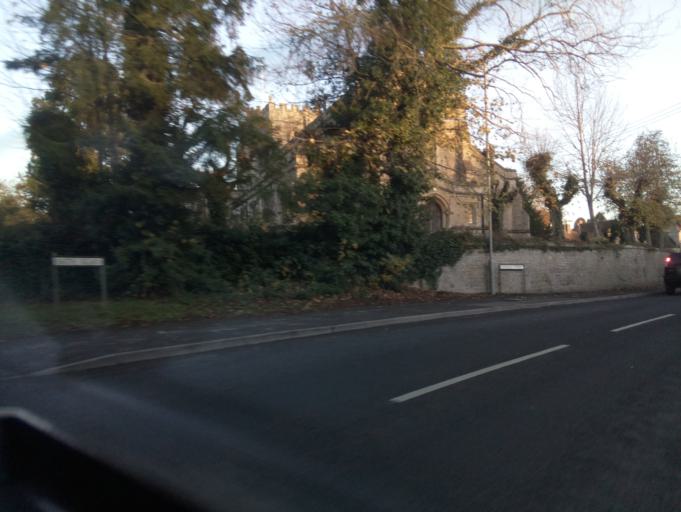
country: GB
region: England
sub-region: Wiltshire
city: Warminster
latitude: 51.2087
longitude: -2.1894
